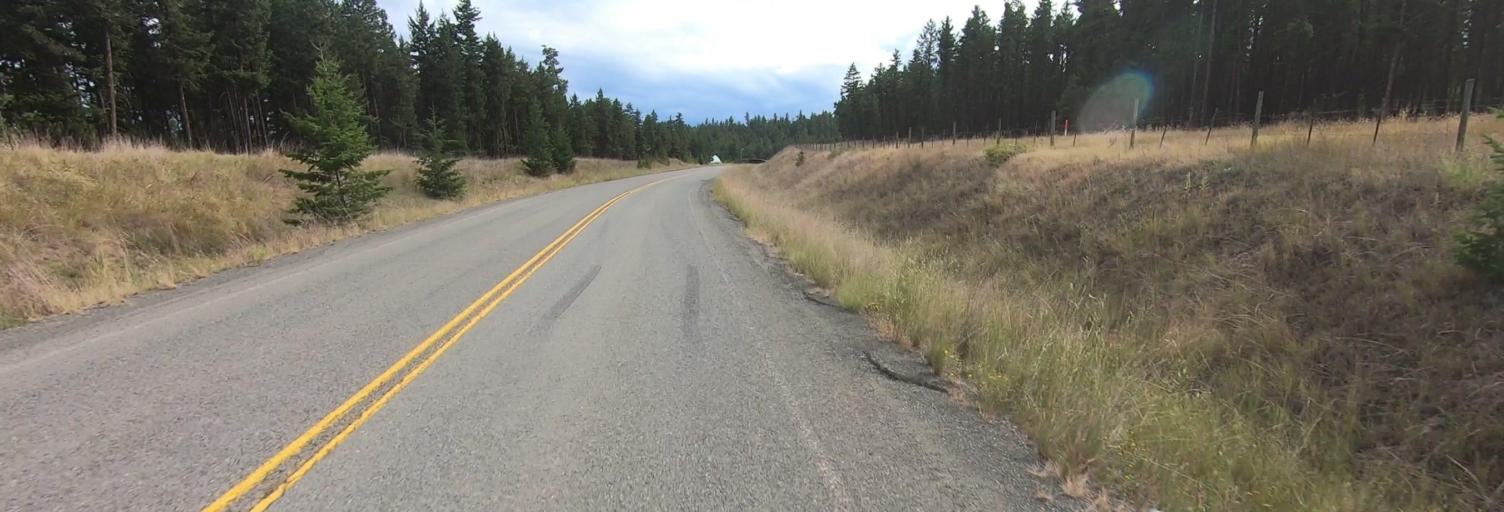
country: CA
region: British Columbia
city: Kamloops
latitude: 50.6191
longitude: -120.4740
